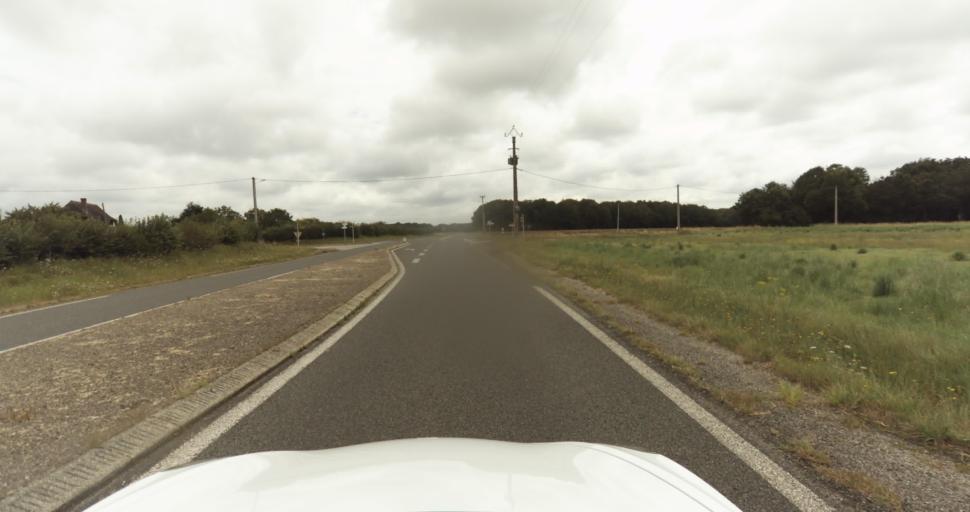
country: FR
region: Haute-Normandie
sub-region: Departement de l'Eure
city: Saint-Sebastien-de-Morsent
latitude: 49.0338
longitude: 1.0646
